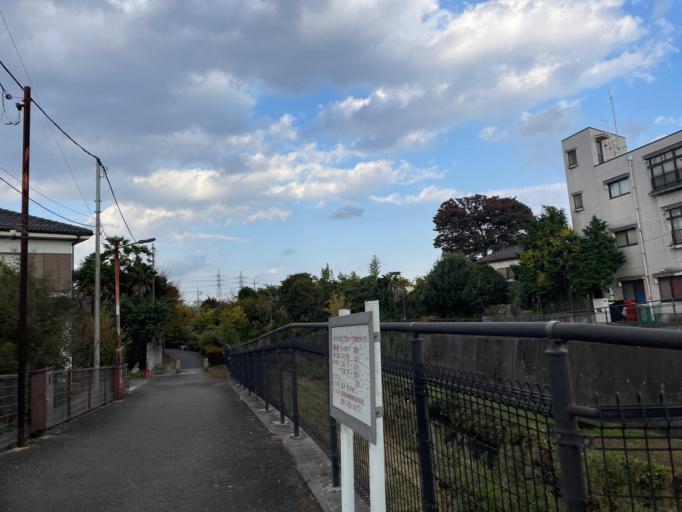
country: JP
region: Tokyo
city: Hino
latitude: 35.7264
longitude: 139.3873
